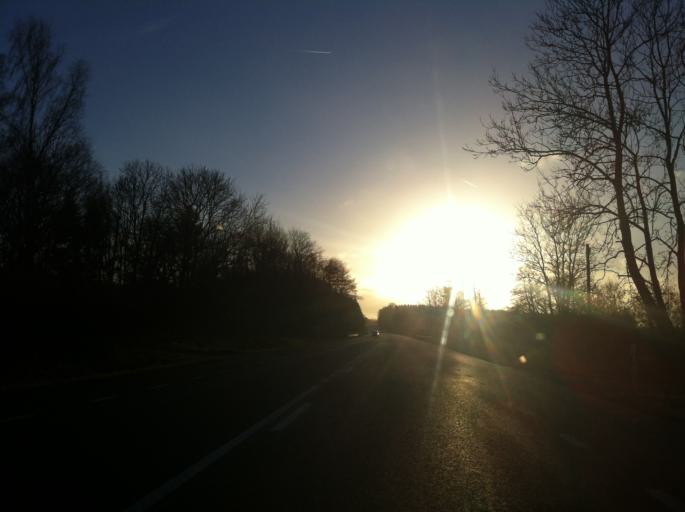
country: SE
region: Skane
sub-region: Hassleholms Kommun
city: Tormestorp
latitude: 56.0973
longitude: 13.7747
